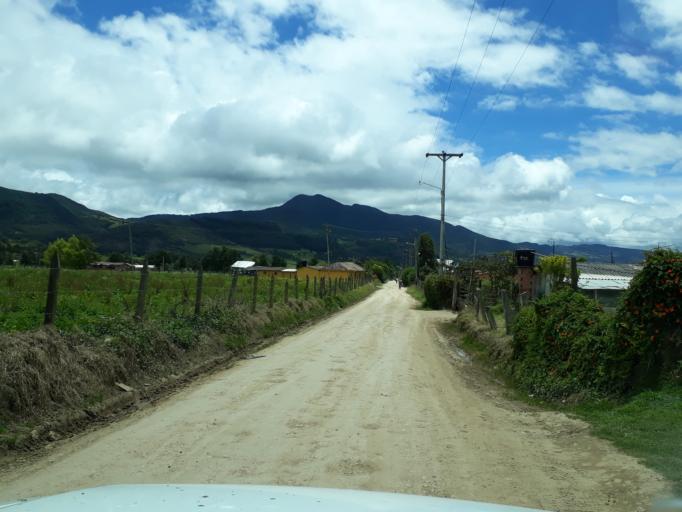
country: CO
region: Cundinamarca
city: Guasca
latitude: 4.8387
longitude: -73.9010
